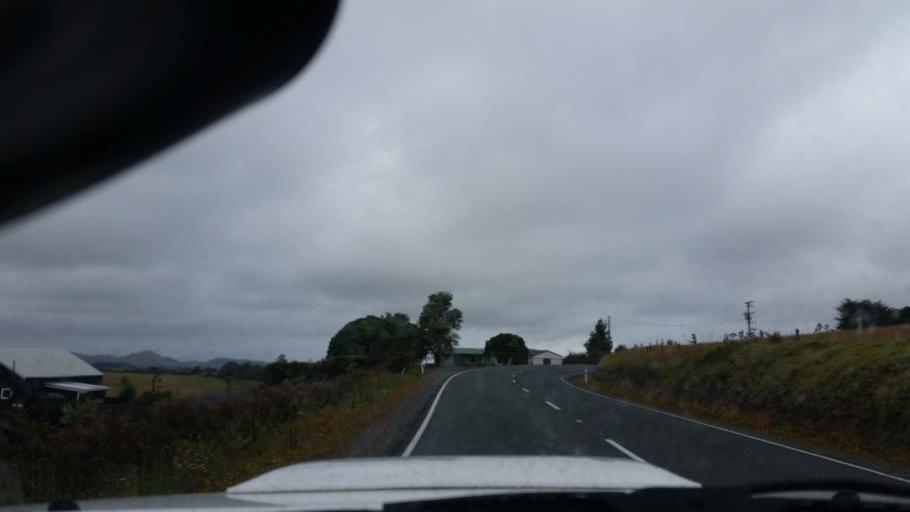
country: NZ
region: Auckland
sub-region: Auckland
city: Wellsford
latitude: -36.1319
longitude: 174.5306
